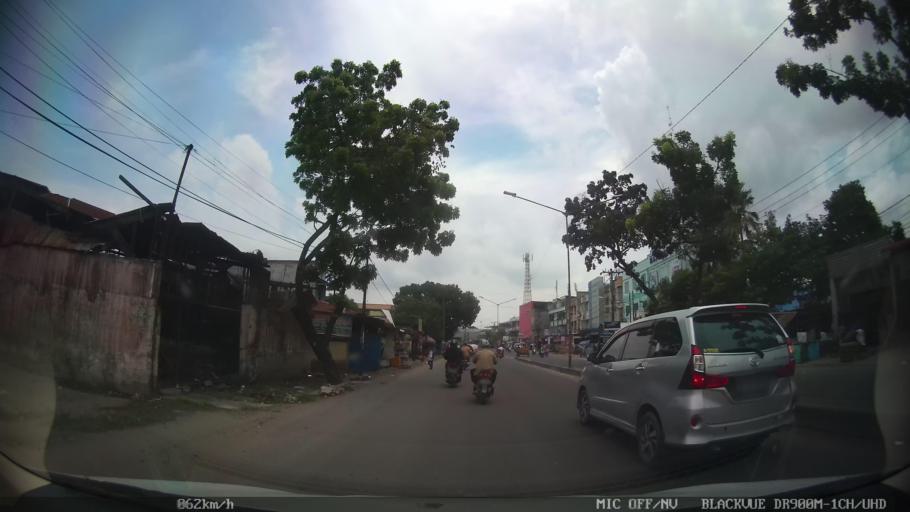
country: ID
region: North Sumatra
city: Labuhan Deli
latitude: 3.6980
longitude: 98.6744
